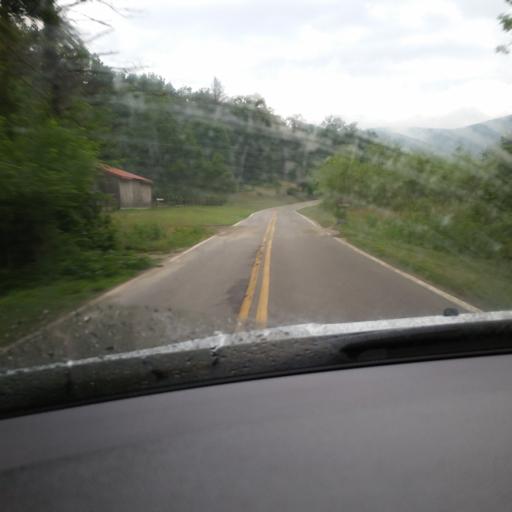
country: US
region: North Carolina
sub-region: Yancey County
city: Burnsville
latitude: 35.8314
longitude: -82.1946
